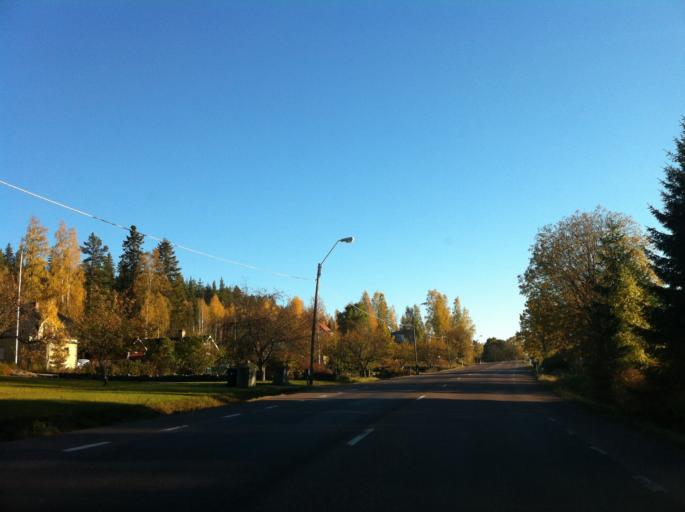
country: SE
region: Dalarna
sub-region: Faluns Kommun
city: Grycksbo
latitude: 60.6988
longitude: 15.4801
